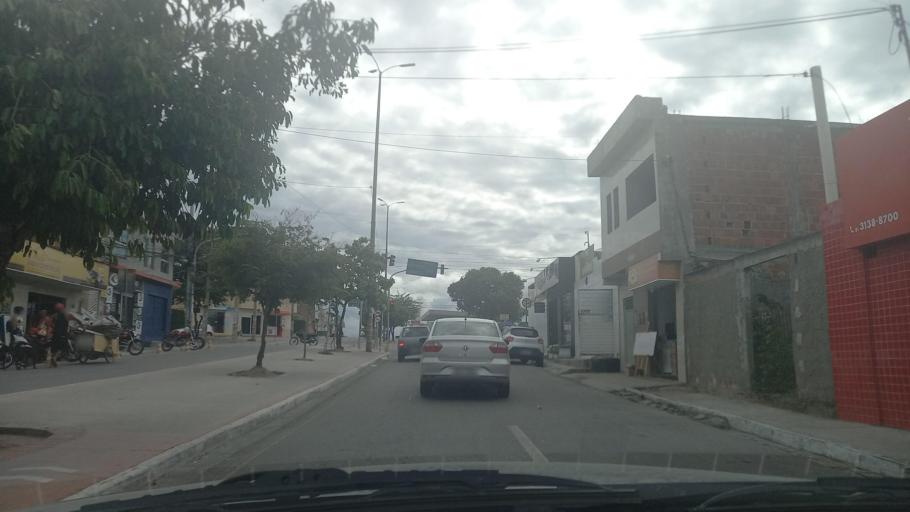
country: BR
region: Pernambuco
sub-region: Caruaru
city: Caruaru
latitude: -8.2745
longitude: -35.9909
